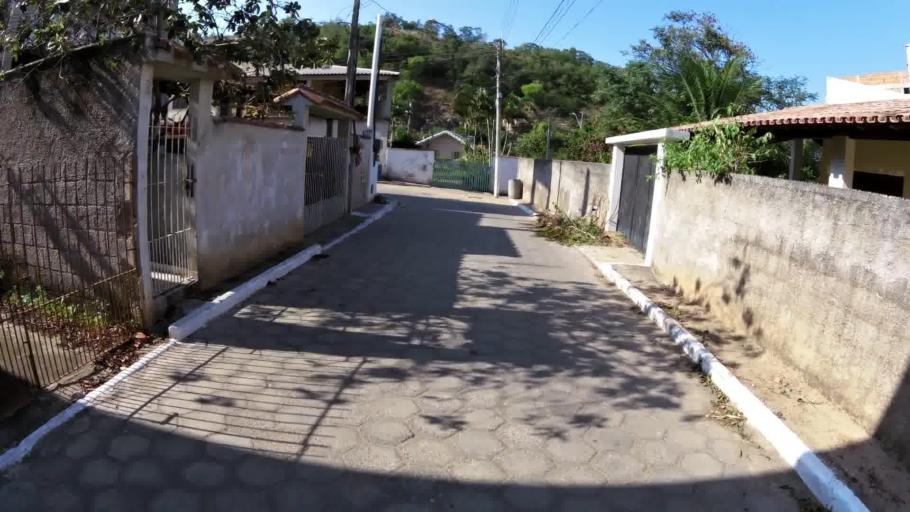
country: BR
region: Espirito Santo
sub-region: Piuma
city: Piuma
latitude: -20.8887
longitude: -40.7728
